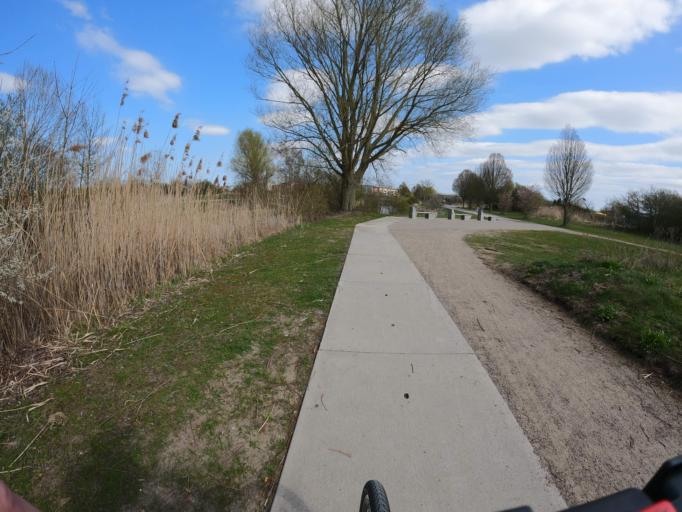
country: DE
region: Schleswig-Holstein
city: Oststeinbek
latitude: 53.4848
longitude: 10.1404
